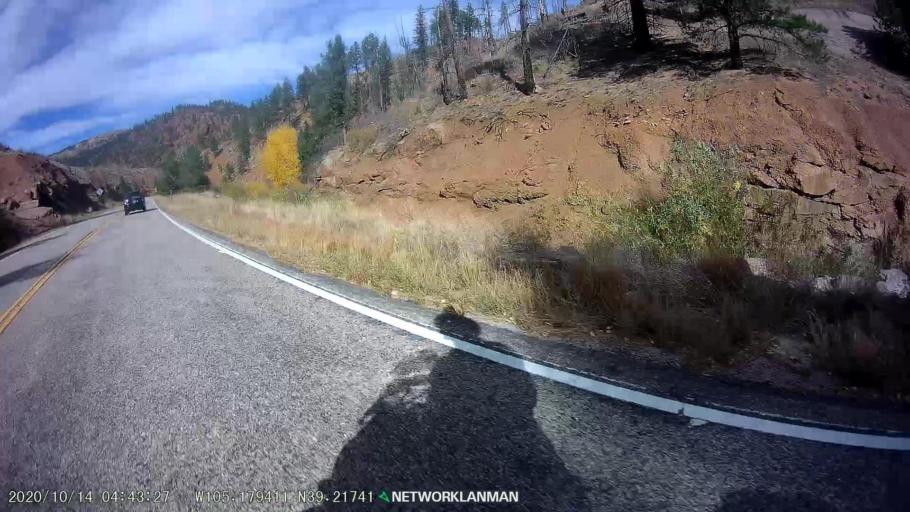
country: US
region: Colorado
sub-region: Douglas County
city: Perry Park
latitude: 39.2175
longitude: -105.1794
